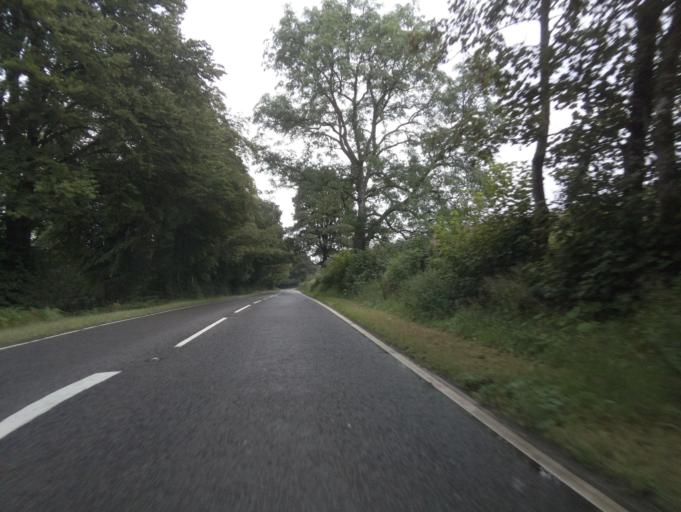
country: GB
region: Scotland
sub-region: Dumfries and Galloway
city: Moffat
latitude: 55.2536
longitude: -3.4586
